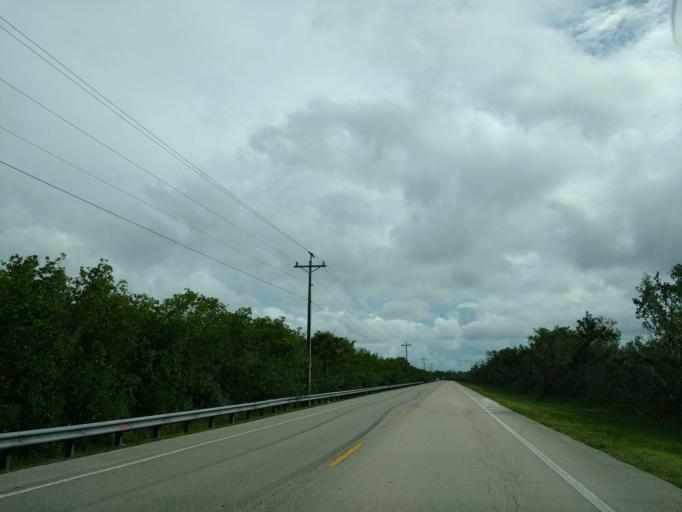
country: US
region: Florida
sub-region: Collier County
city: Marco
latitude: 25.8914
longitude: -81.3755
